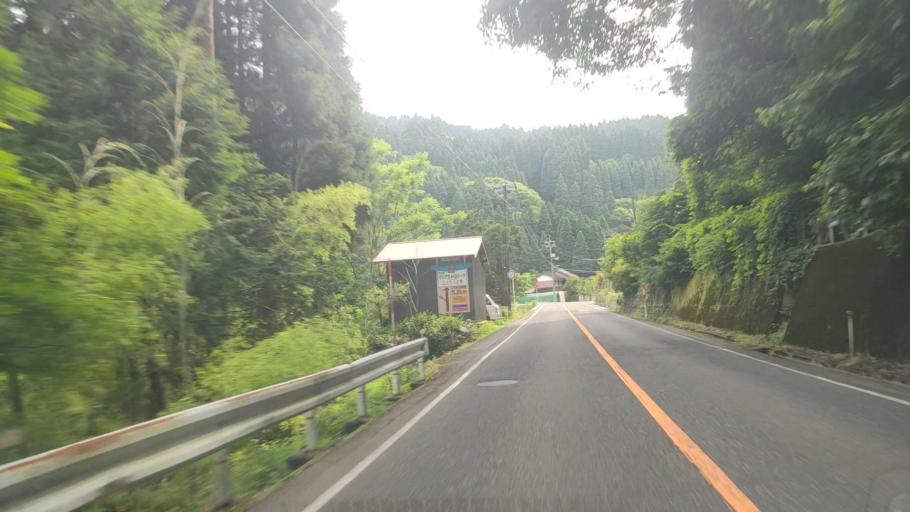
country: JP
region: Tottori
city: Tottori
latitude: 35.3331
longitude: 134.1324
